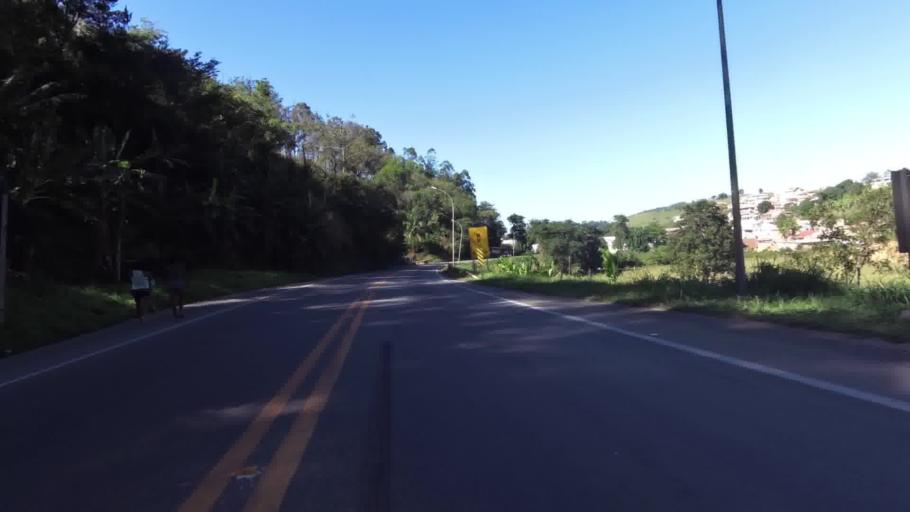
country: BR
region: Espirito Santo
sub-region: Iconha
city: Iconha
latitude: -20.7956
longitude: -40.8161
